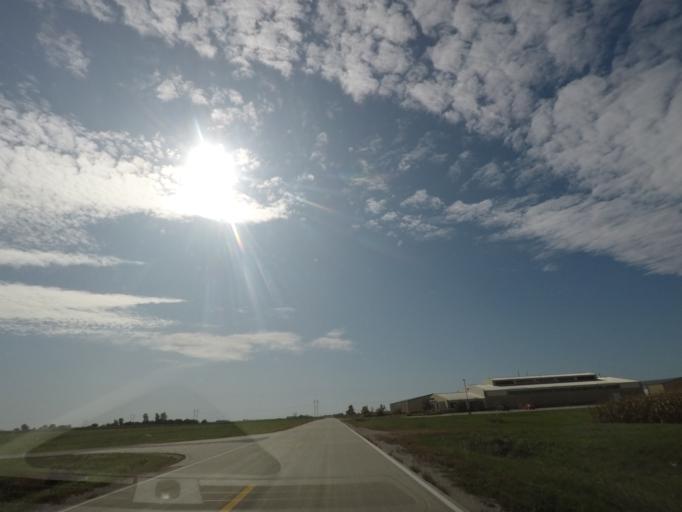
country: US
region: Iowa
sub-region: Boone County
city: Boone
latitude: 42.0209
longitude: -93.7768
